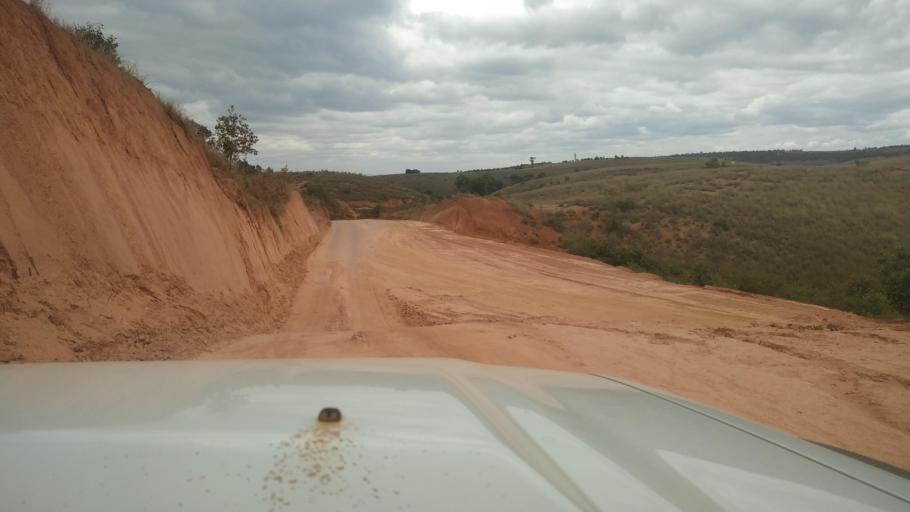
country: MG
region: Alaotra Mangoro
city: Ambatondrazaka
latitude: -17.9683
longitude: 48.2558
